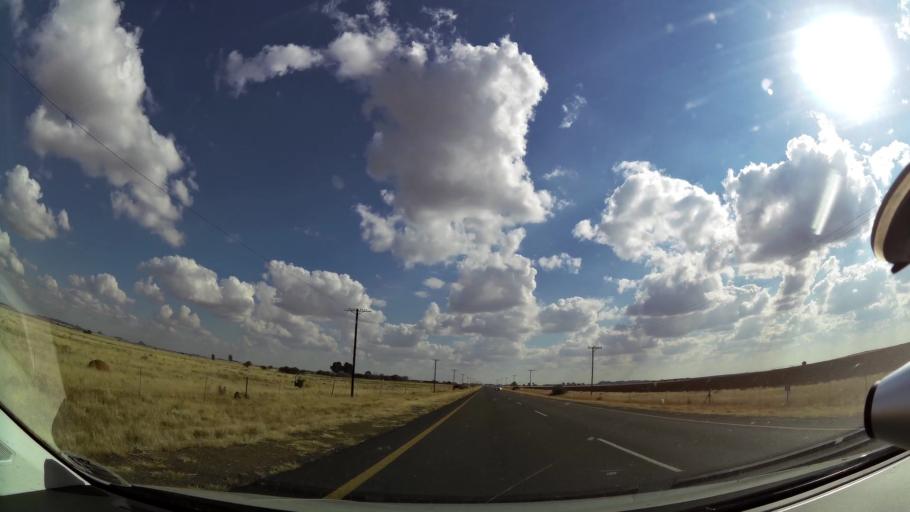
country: ZA
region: Orange Free State
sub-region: Xhariep District Municipality
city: Koffiefontein
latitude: -29.1286
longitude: 25.4974
